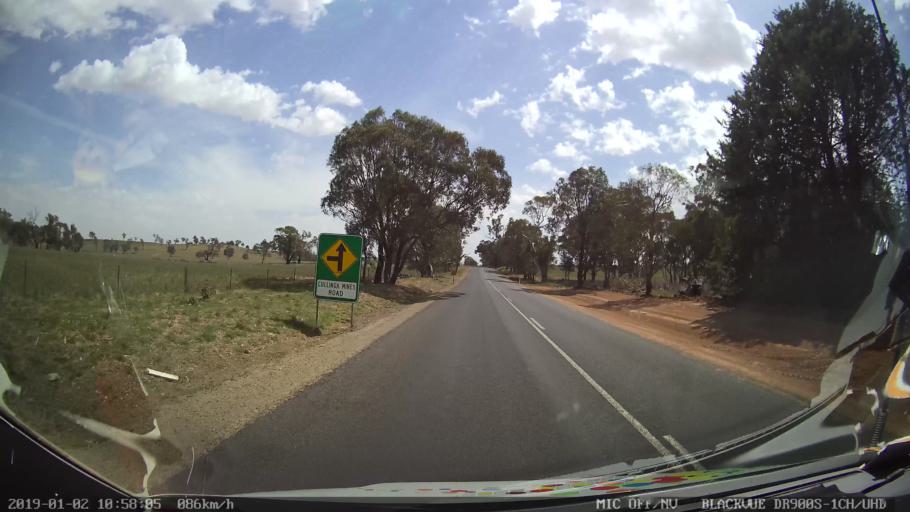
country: AU
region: New South Wales
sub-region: Cootamundra
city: Cootamundra
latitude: -34.6281
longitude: 148.2881
